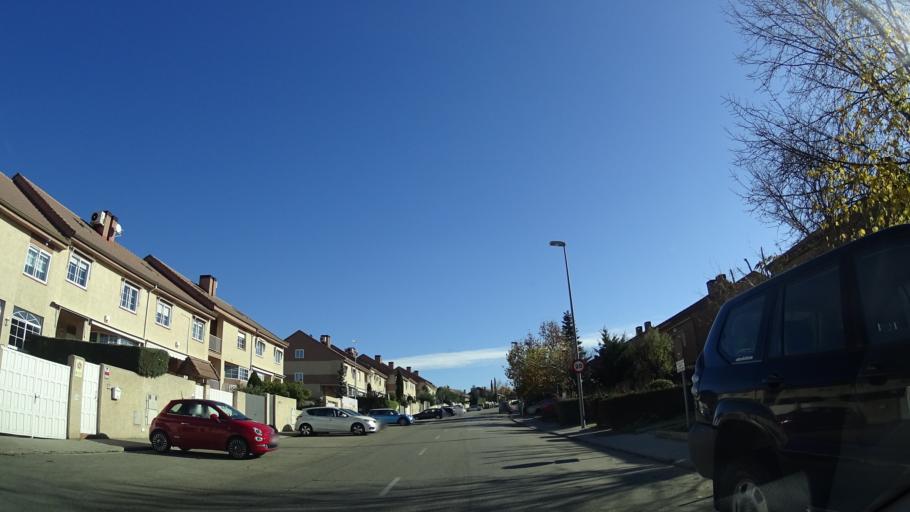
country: ES
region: Madrid
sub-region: Provincia de Madrid
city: Las Matas
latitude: 40.5249
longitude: -3.9149
